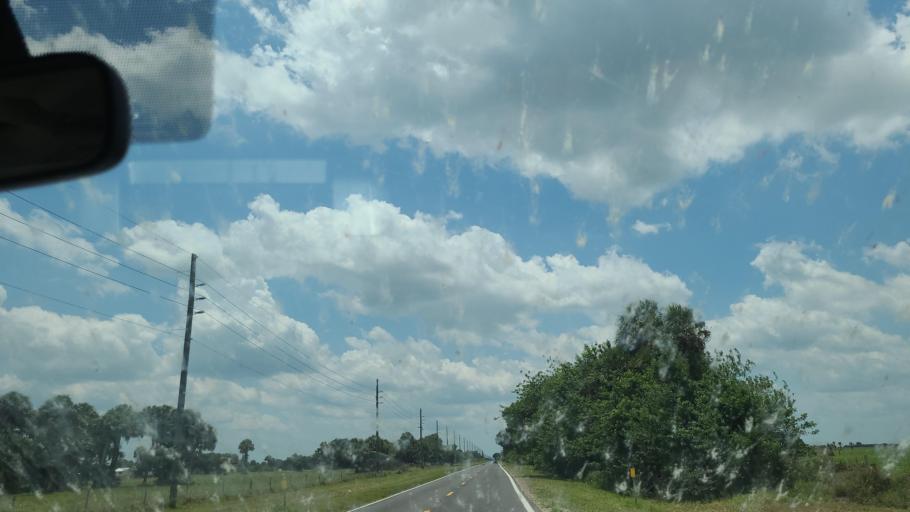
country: US
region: Florida
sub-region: Glades County
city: Buckhead Ridge
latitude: 27.2222
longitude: -81.0947
